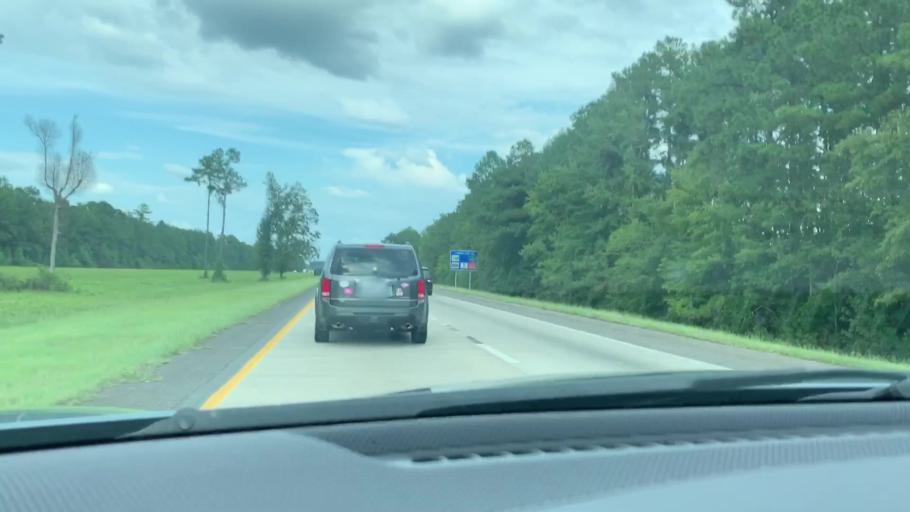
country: US
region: South Carolina
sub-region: Colleton County
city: Walterboro
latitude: 32.8656
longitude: -80.7241
